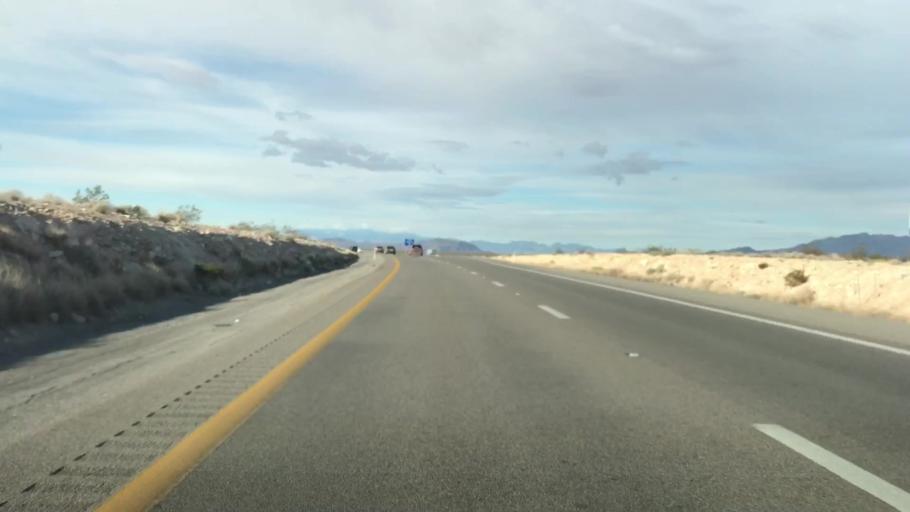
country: US
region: Nevada
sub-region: Clark County
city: Bunkerville
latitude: 36.7794
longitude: -114.2634
